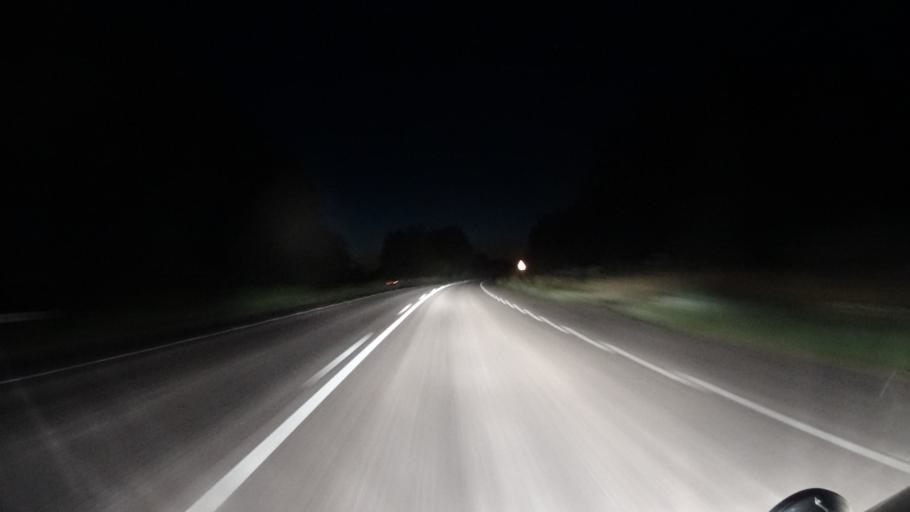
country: SE
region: OEstergoetland
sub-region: Vadstena Kommun
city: Herrestad
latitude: 58.2802
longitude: 14.7588
